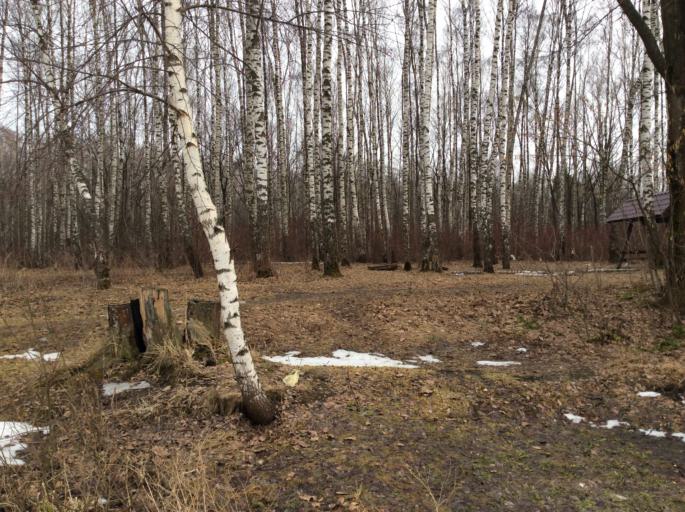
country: RU
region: Moskovskaya
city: Medvezh'i Ozera
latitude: 55.8695
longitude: 38.0050
